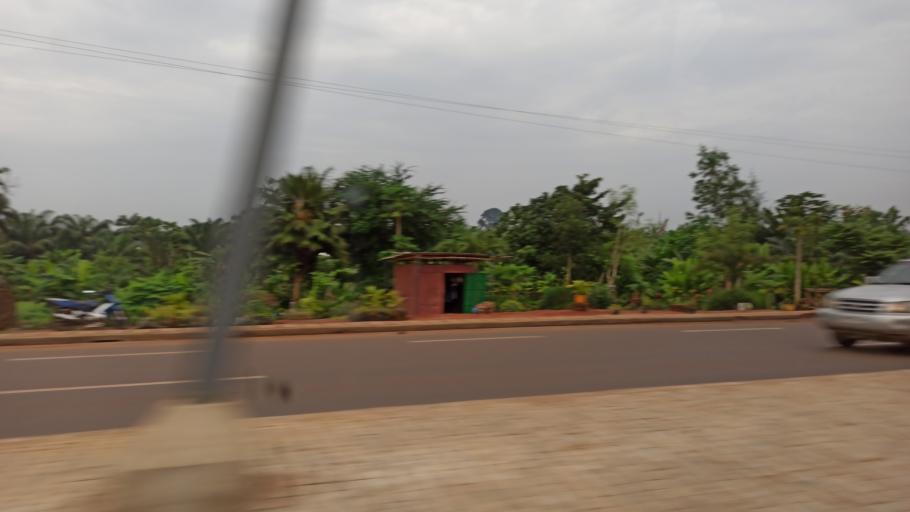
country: BJ
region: Queme
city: Porto-Novo
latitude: 6.5304
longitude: 2.6000
